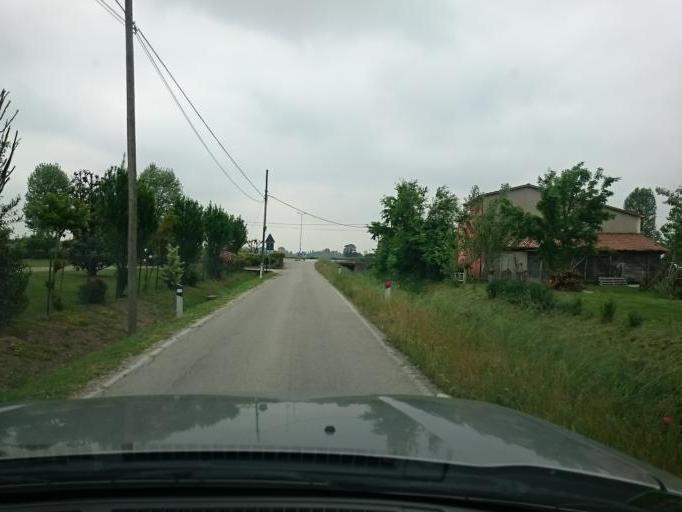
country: IT
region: Veneto
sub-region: Provincia di Padova
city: Cartura
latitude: 45.2907
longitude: 11.8688
